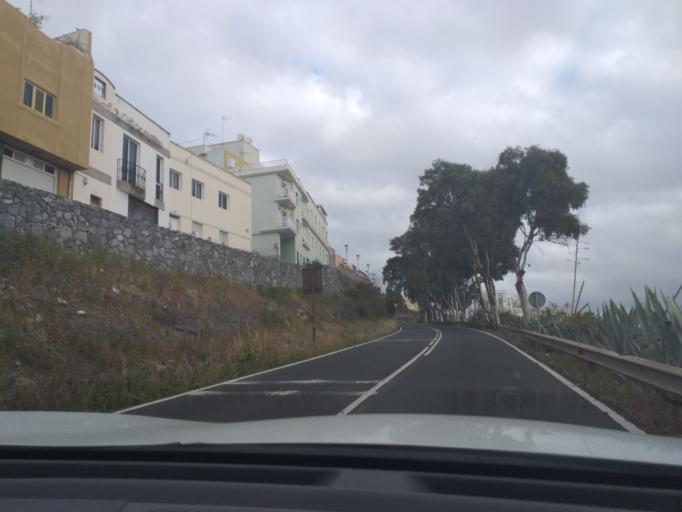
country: ES
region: Canary Islands
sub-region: Provincia de Las Palmas
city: Arucas
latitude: 28.1097
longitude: -15.5069
